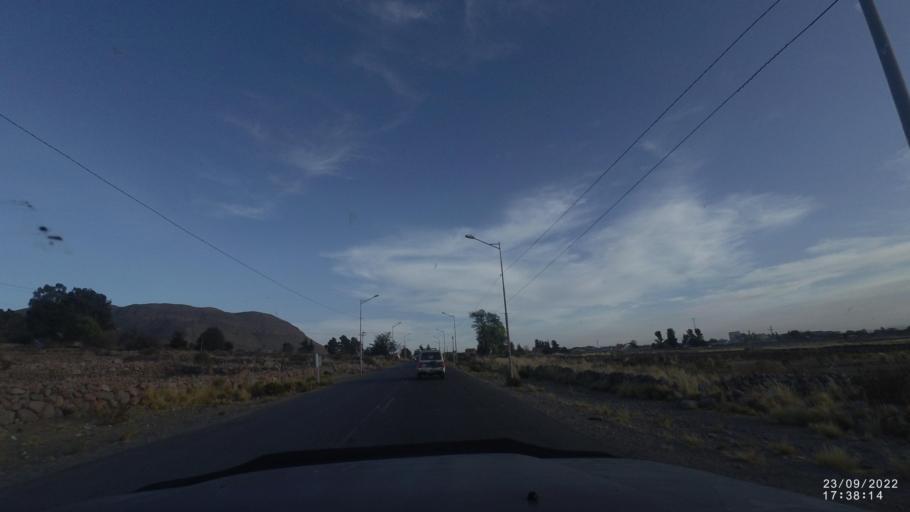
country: BO
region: Oruro
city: Challapata
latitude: -19.0031
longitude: -66.7767
